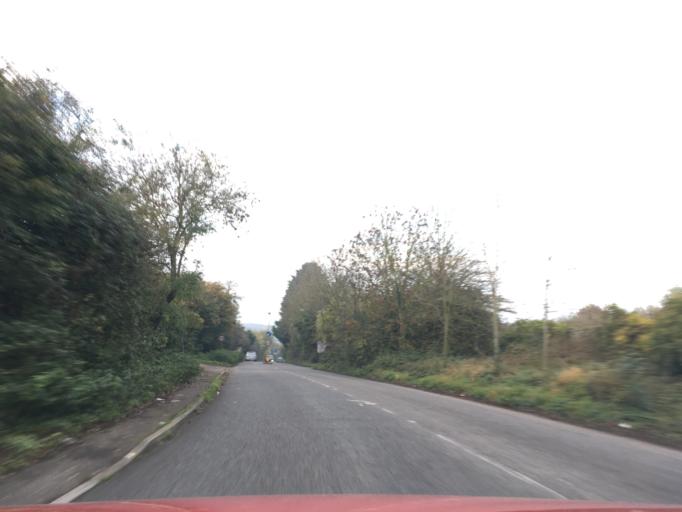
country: GB
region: England
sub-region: South Gloucestershire
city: Siston
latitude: 51.4818
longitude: -2.4593
